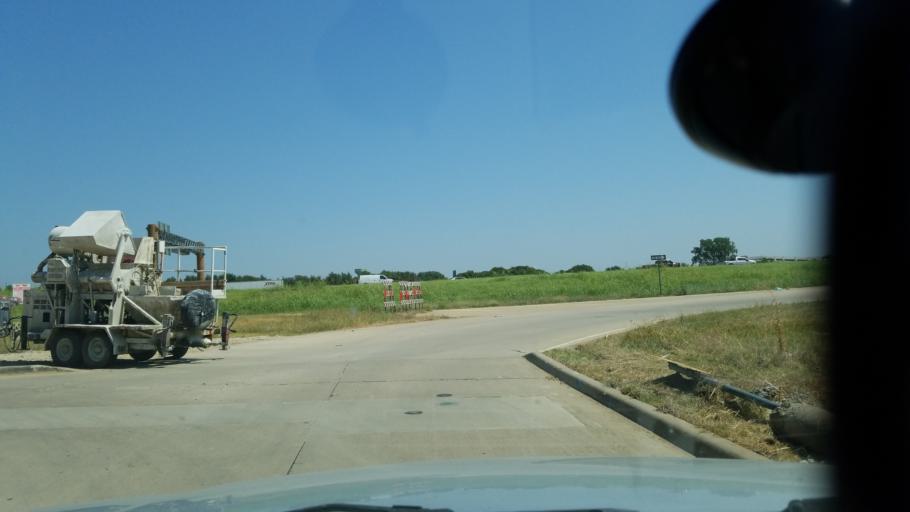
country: US
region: Texas
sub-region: Dallas County
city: Farmers Branch
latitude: 32.9065
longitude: -96.9250
